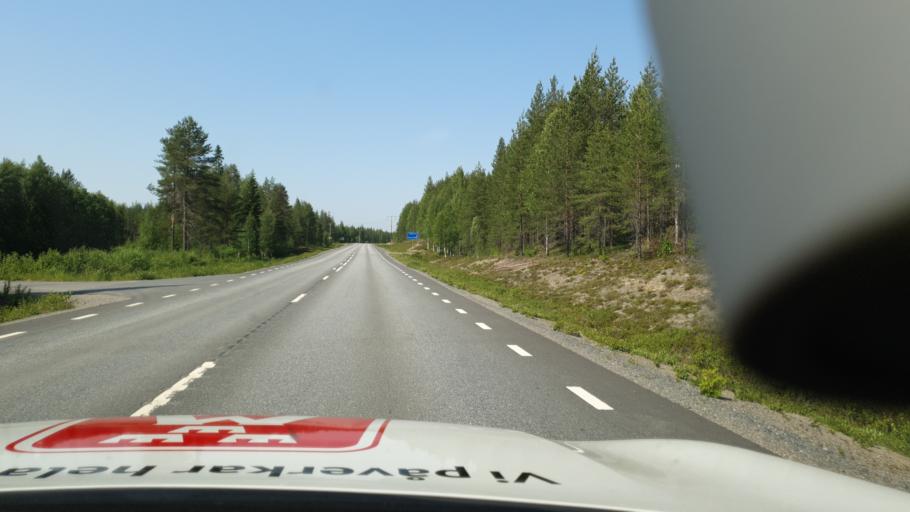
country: SE
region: Vaesterbotten
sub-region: Norsjo Kommun
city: Norsjoe
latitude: 64.9735
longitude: 19.7299
